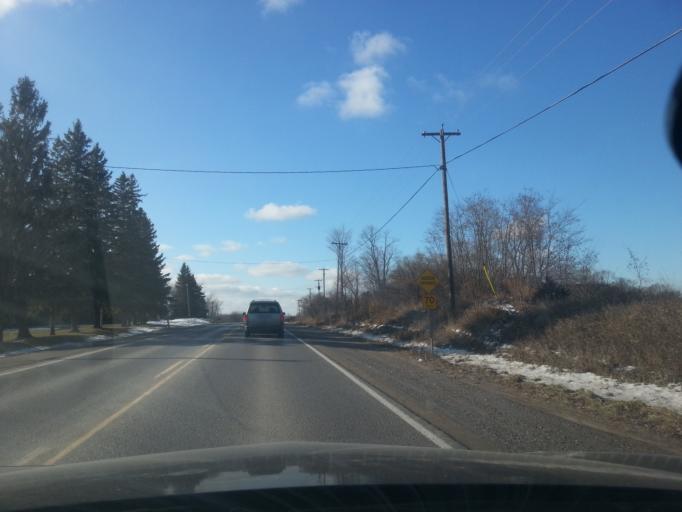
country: CA
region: Ontario
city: Peterborough
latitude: 44.2689
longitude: -78.4002
